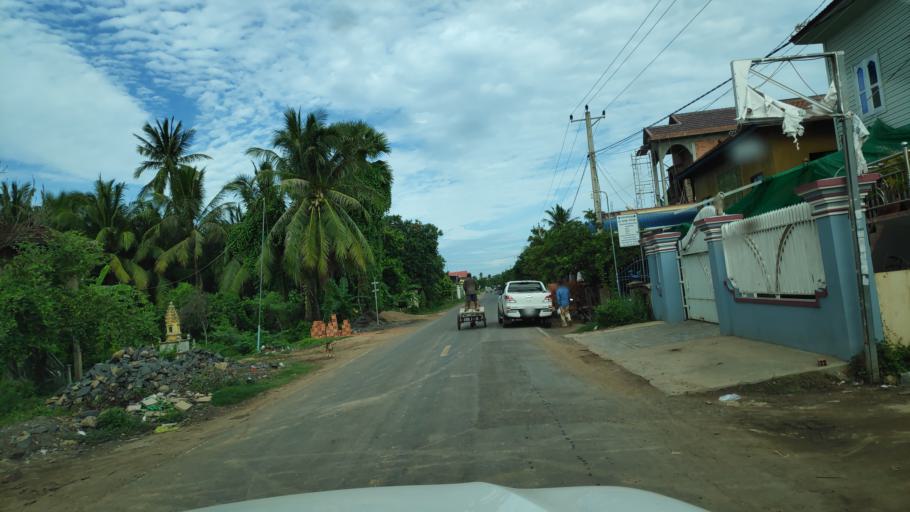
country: KH
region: Kampong Cham
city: Kampong Cham
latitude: 11.9466
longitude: 105.2475
